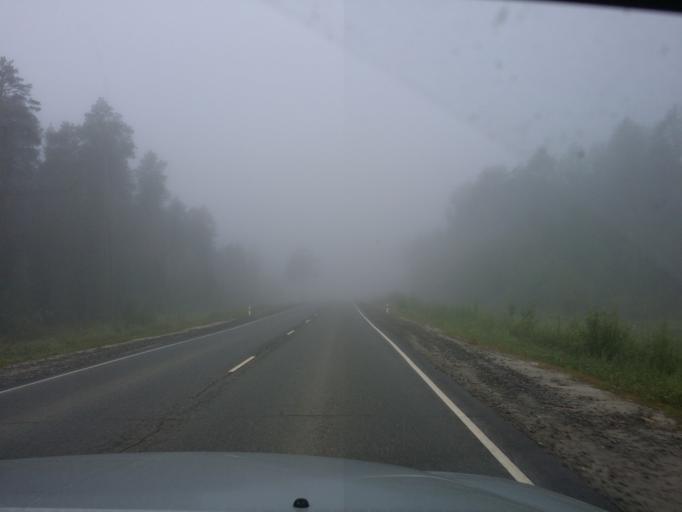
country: RU
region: Khanty-Mansiyskiy Avtonomnyy Okrug
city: Gornopravdinsk
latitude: 59.6480
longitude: 69.9077
